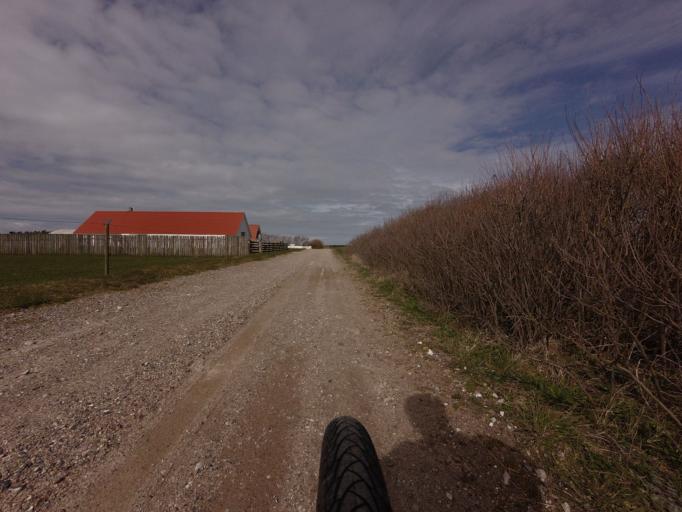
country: DK
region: North Denmark
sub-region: Jammerbugt Kommune
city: Pandrup
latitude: 57.3869
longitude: 9.7365
